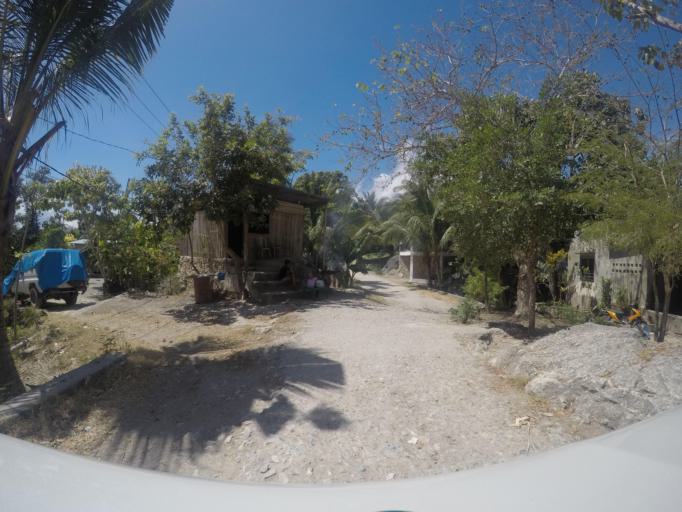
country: TL
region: Baucau
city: Baucau
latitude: -8.4655
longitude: 126.4567
